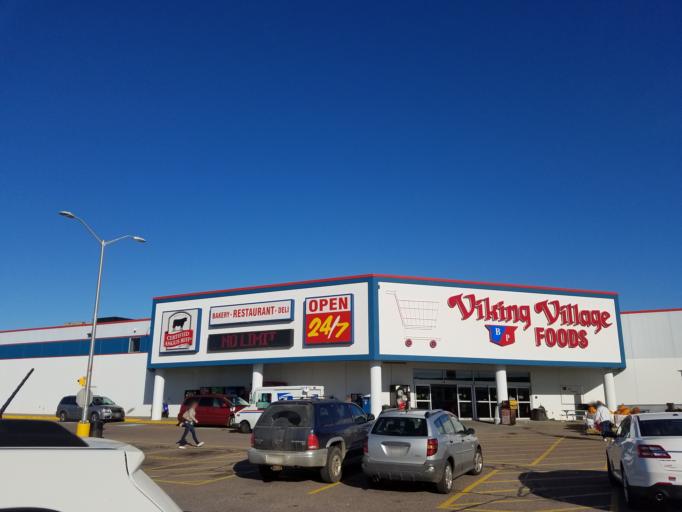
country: US
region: Wisconsin
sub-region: Sauk County
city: Reedsburg
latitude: 43.5344
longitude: -89.9826
